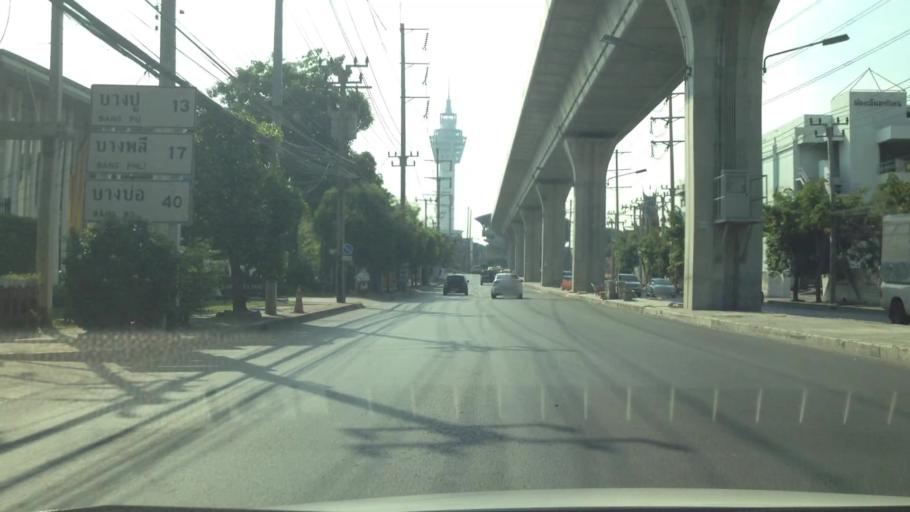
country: TH
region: Samut Prakan
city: Samut Prakan
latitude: 13.6052
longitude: 100.5962
